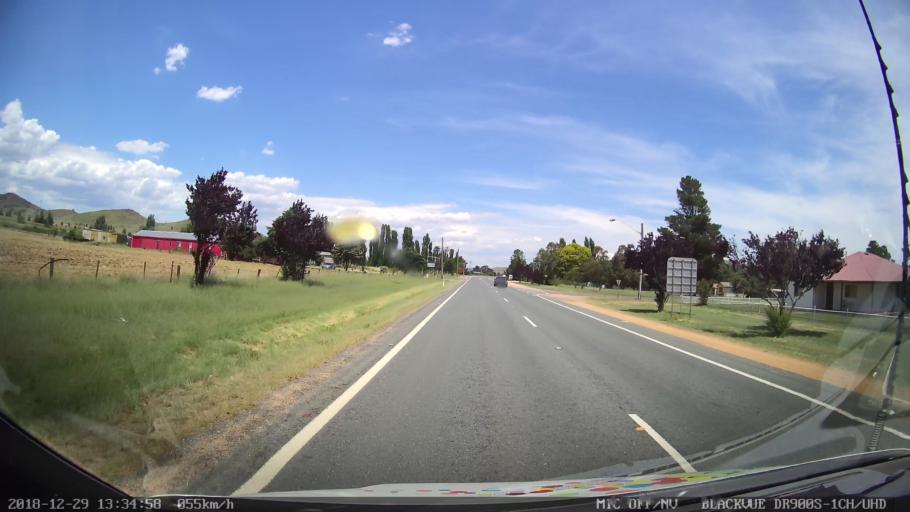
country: AU
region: New South Wales
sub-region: Cooma-Monaro
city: Cooma
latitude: -35.9567
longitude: 149.1489
